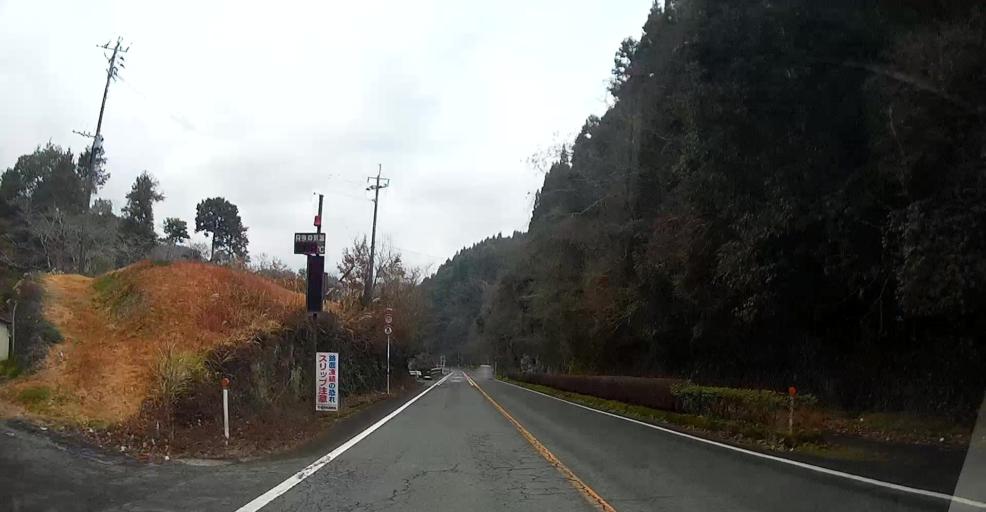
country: JP
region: Kumamoto
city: Matsubase
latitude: 32.6276
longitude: 130.8869
